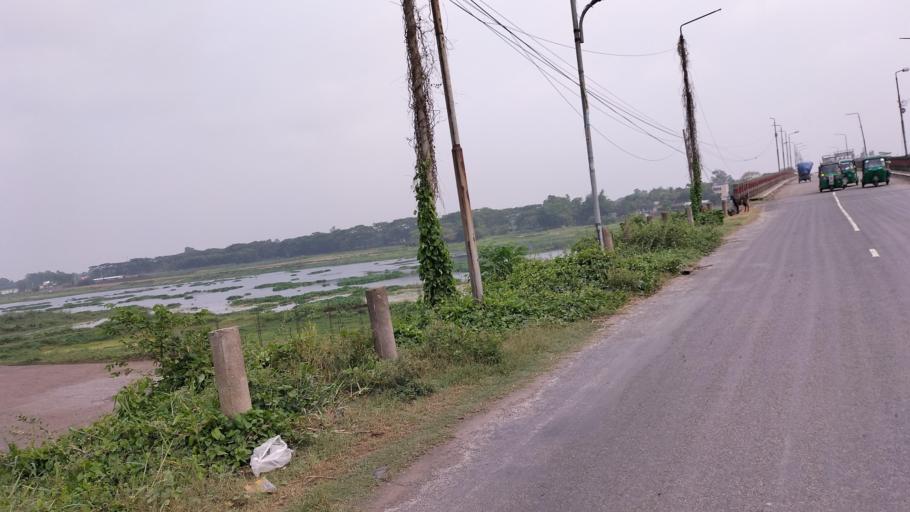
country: BD
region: Dhaka
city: Azimpur
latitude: 23.7560
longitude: 90.2494
